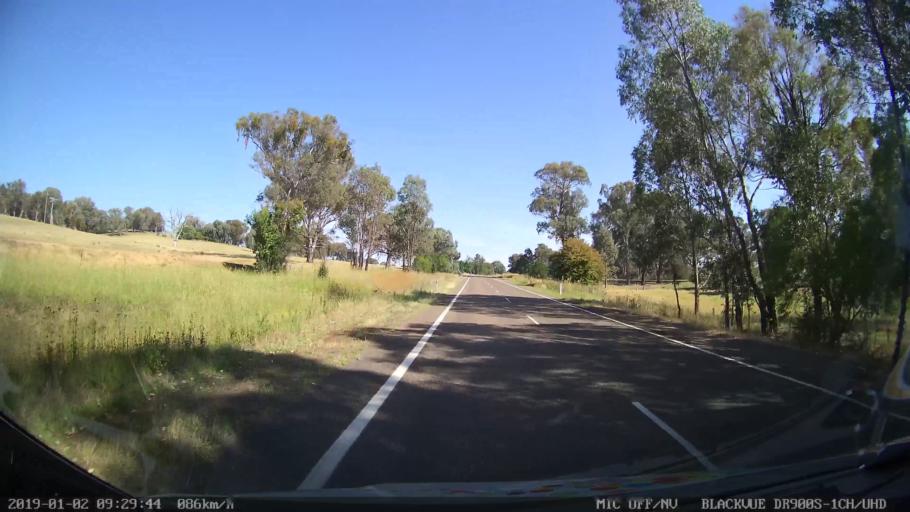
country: AU
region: New South Wales
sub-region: Tumut Shire
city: Tumut
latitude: -35.3354
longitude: 148.2399
